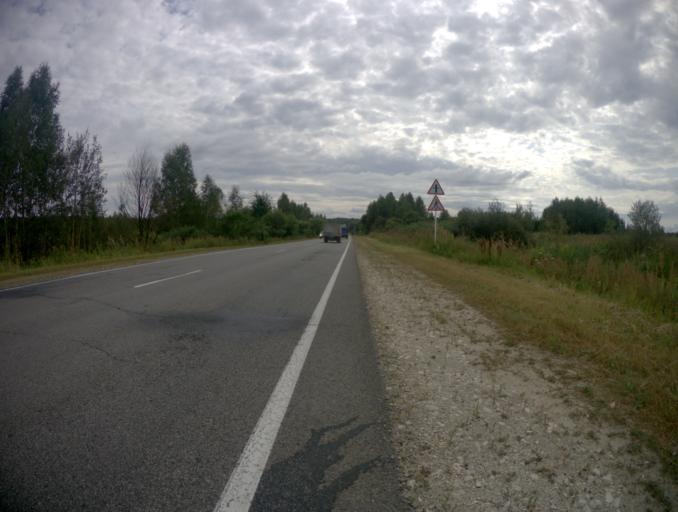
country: RU
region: Vladimir
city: Golovino
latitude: 55.9555
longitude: 40.5676
